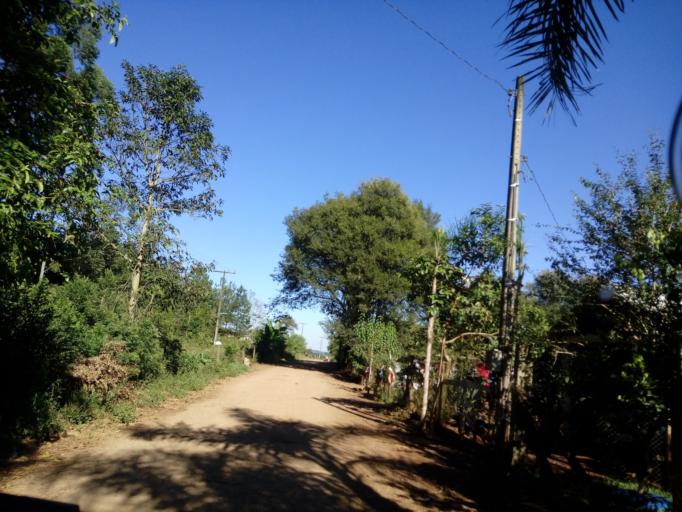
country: BR
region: Santa Catarina
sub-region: Chapeco
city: Chapeco
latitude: -27.1933
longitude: -52.7470
